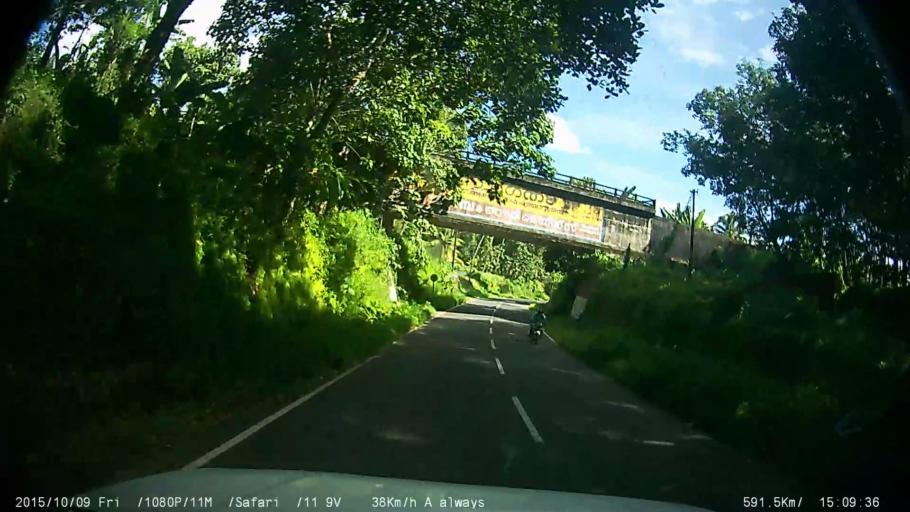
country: IN
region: Kerala
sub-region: Ernakulam
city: Piravam
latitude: 9.8849
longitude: 76.5730
